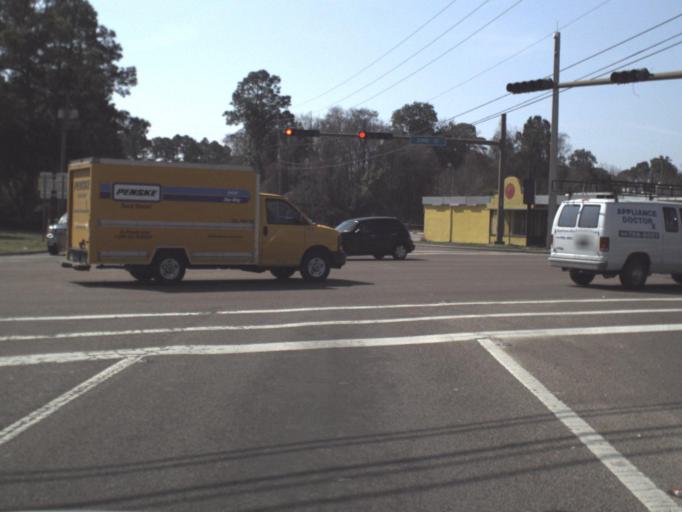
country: US
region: Florida
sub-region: Bay County
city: Pretty Bayou
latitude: 30.1899
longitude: -85.7006
